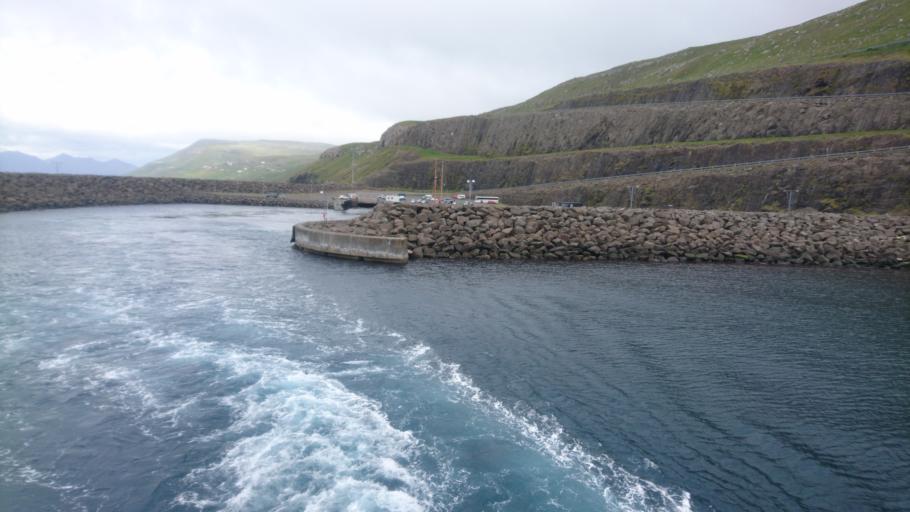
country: FO
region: Streymoy
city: Argir
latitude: 61.9604
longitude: -6.8167
